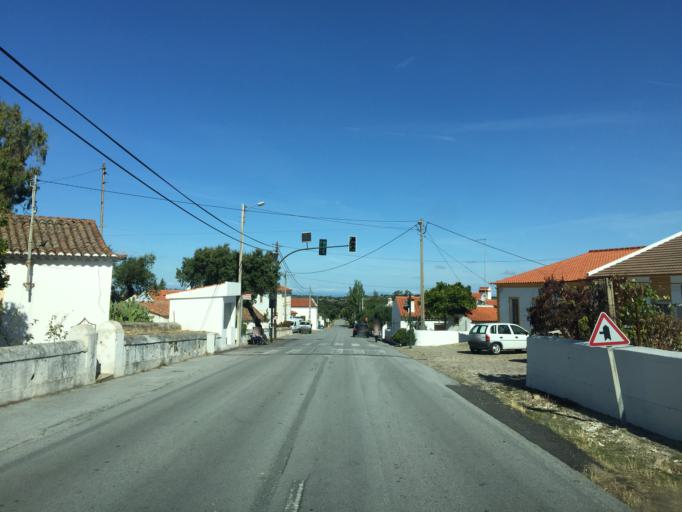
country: PT
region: Portalegre
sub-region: Marvao
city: Marvao
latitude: 39.4335
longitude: -7.3627
